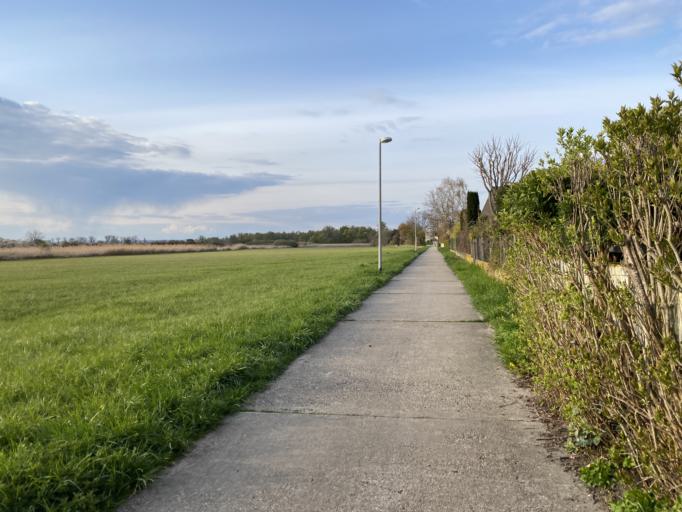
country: DE
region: Hesse
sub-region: Regierungsbezirk Darmstadt
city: Gross-Gerau
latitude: 49.9078
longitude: 8.4720
